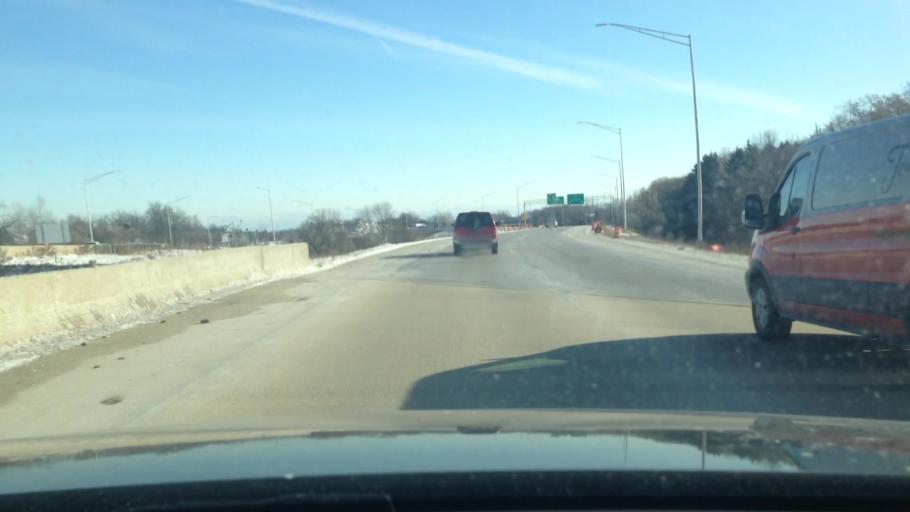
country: US
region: Wisconsin
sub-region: Waukesha County
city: New Berlin
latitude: 42.9586
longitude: -88.0789
